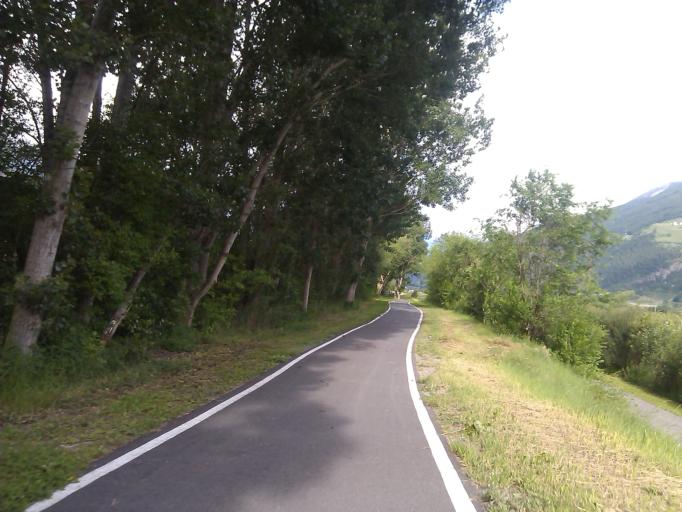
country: IT
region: Trentino-Alto Adige
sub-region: Bolzano
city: Lasa
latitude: 46.6195
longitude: 10.6714
